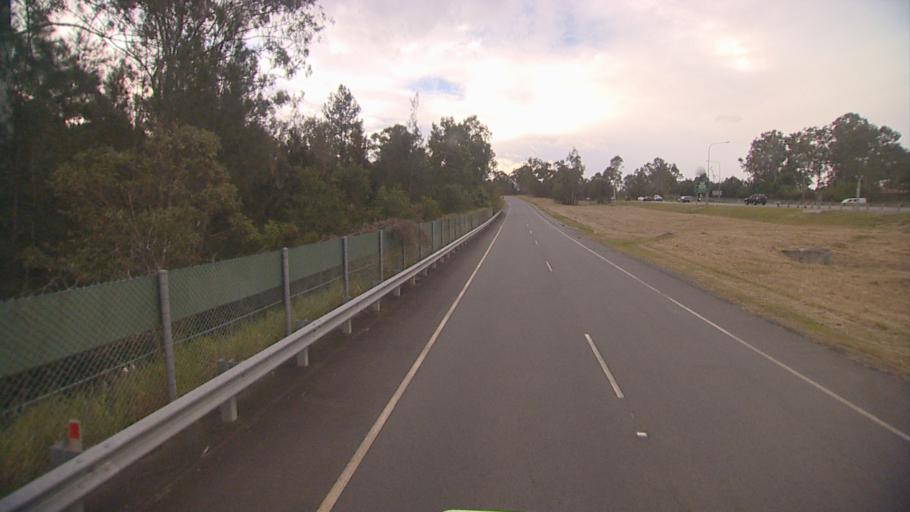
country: AU
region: Queensland
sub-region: Logan
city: Park Ridge South
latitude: -27.7298
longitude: 153.0288
